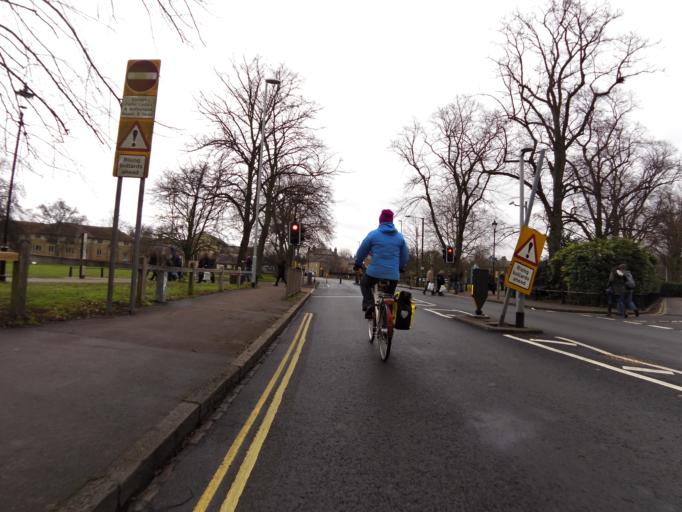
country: GB
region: England
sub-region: Cambridgeshire
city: Cambridge
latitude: 52.2062
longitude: 0.1267
